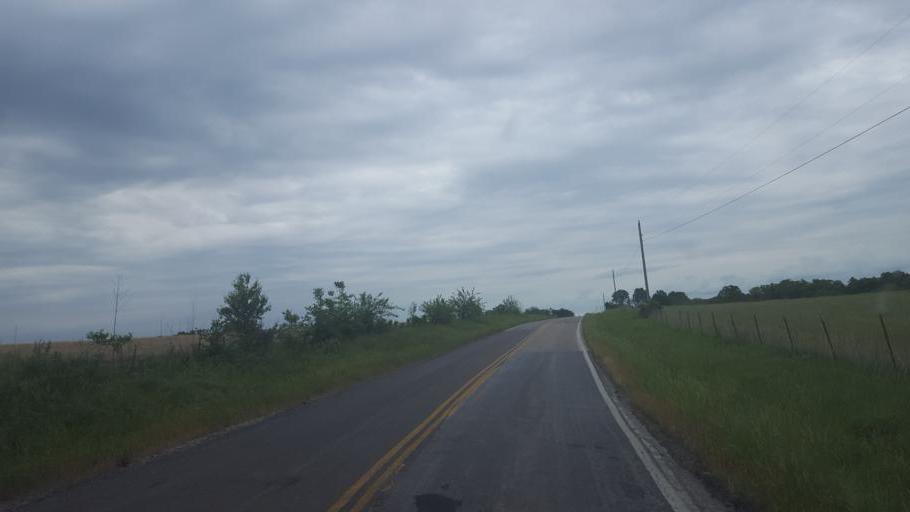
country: US
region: Missouri
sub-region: Moniteau County
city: California
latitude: 38.6719
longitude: -92.5865
